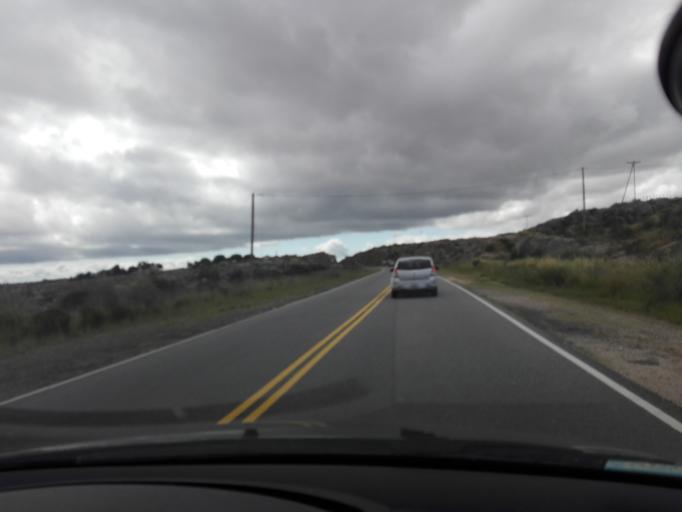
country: AR
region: Cordoba
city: Villa Cura Brochero
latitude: -31.6161
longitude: -64.8982
